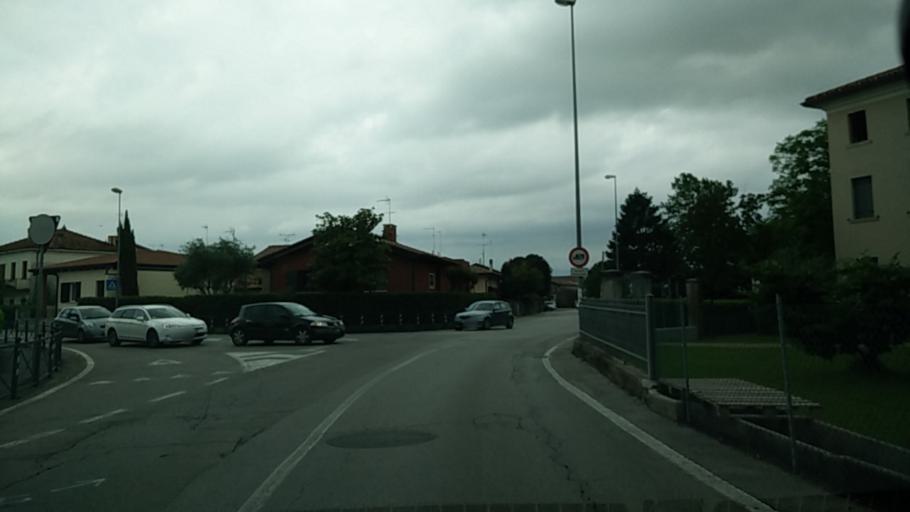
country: IT
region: Veneto
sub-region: Provincia di Treviso
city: Mareno di Piave
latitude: 45.8468
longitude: 12.3526
